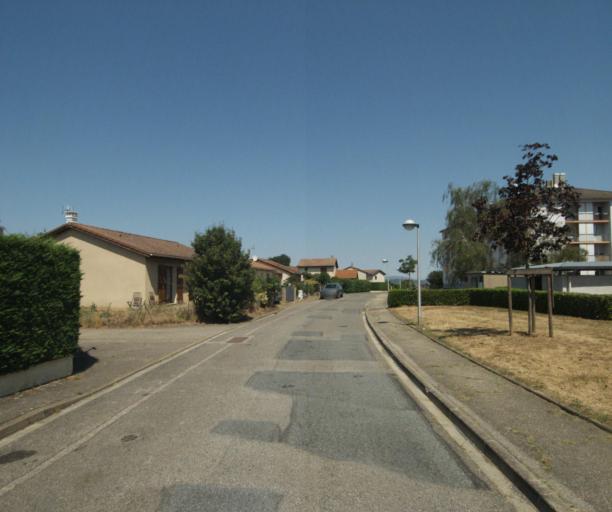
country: FR
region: Rhone-Alpes
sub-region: Departement du Rhone
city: Saint-Pierre-la-Palud
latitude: 45.7906
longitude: 4.6103
